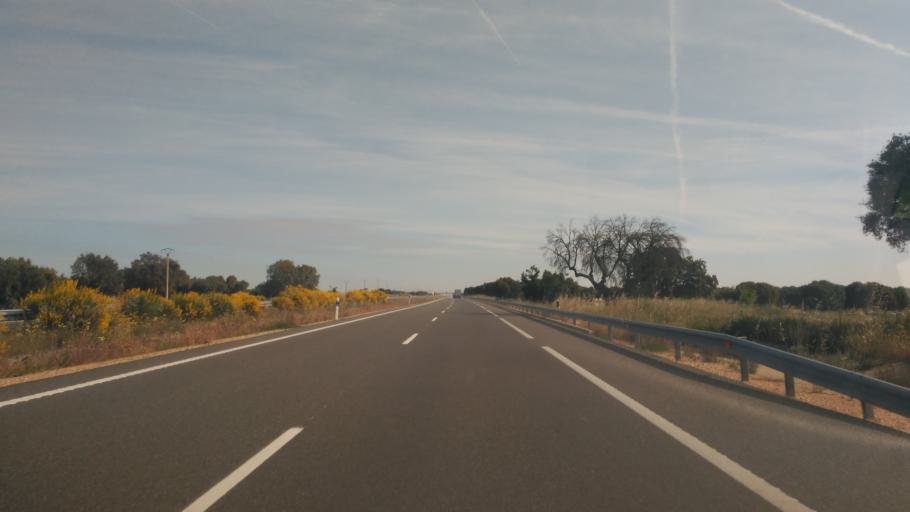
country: ES
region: Castille and Leon
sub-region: Provincia de Salamanca
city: Calzada de Valdunciel
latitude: 41.1424
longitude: -5.6963
